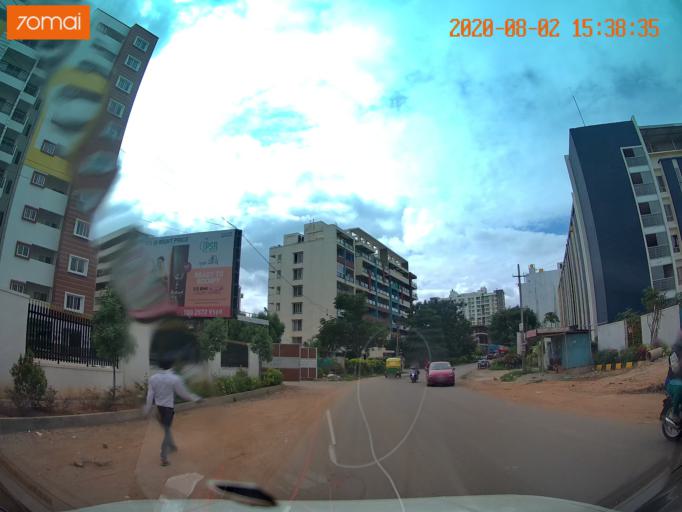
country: IN
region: Karnataka
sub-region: Bangalore Urban
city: Anekal
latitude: 12.8404
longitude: 77.6442
